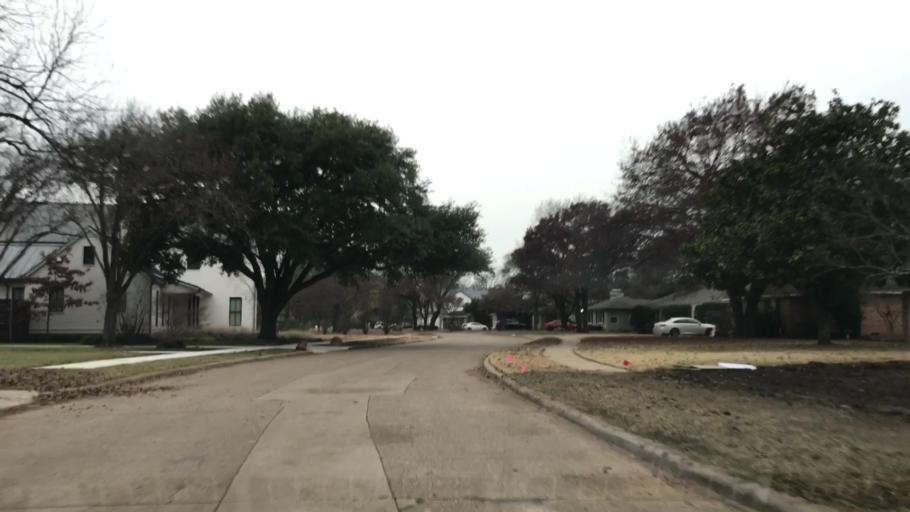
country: US
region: Texas
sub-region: Dallas County
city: University Park
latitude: 32.8670
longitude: -96.8452
